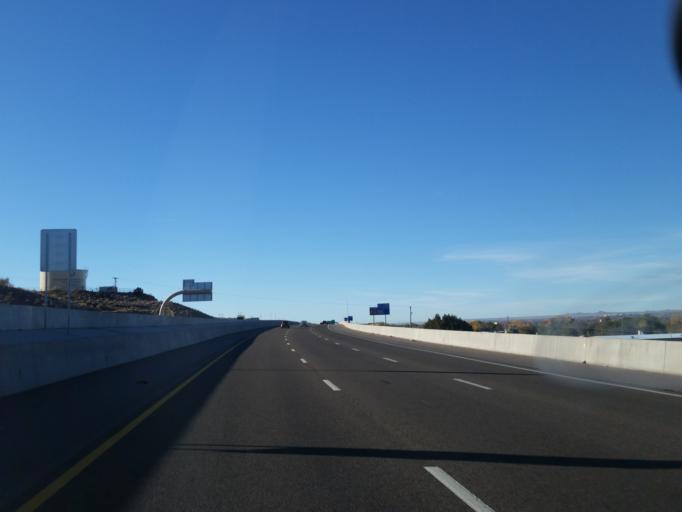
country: US
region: New Mexico
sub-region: Sandoval County
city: Bernalillo
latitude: 35.3054
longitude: -106.5362
